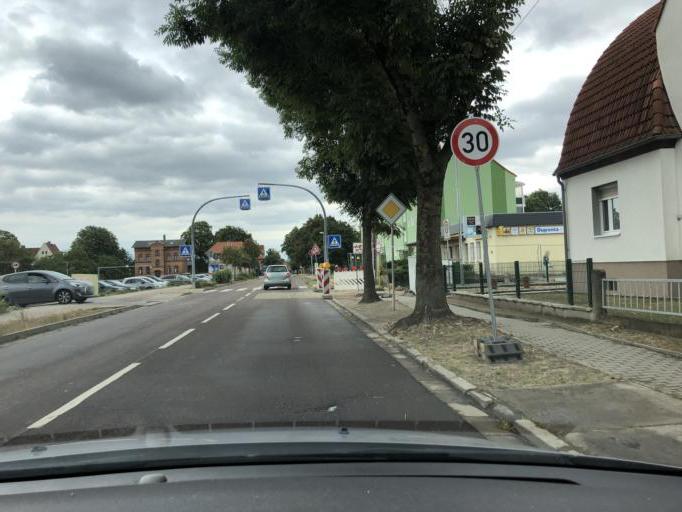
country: DE
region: Saxony-Anhalt
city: Nienburg/Saale
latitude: 51.8381
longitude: 11.7592
